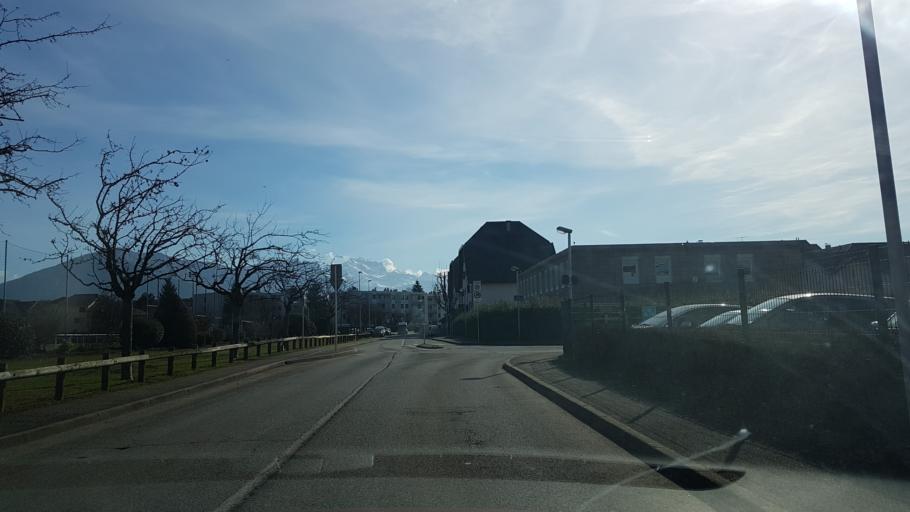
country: FR
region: Rhone-Alpes
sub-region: Departement de la Haute-Savoie
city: Meythet
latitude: 45.9207
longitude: 6.0912
